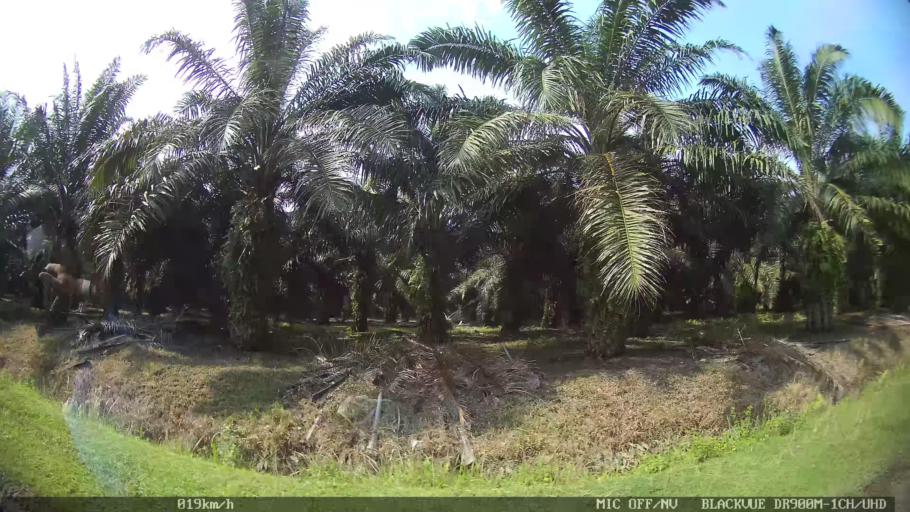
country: ID
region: North Sumatra
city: Binjai
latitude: 3.6427
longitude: 98.5240
